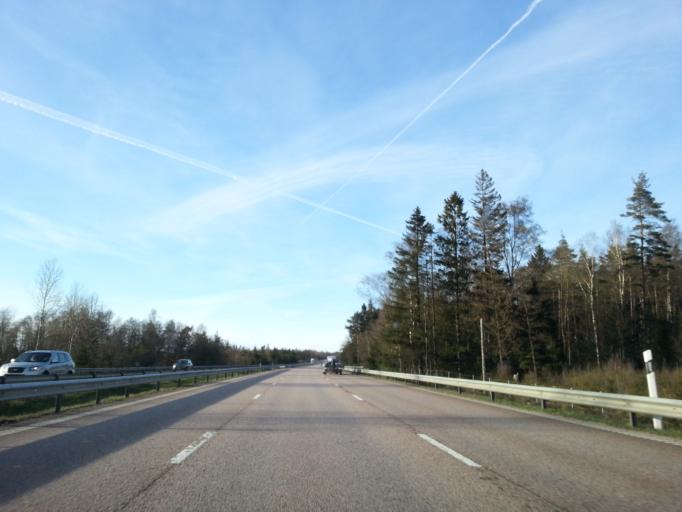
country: SE
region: Skane
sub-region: Bastads Kommun
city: Bastad
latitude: 56.3758
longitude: 12.9343
